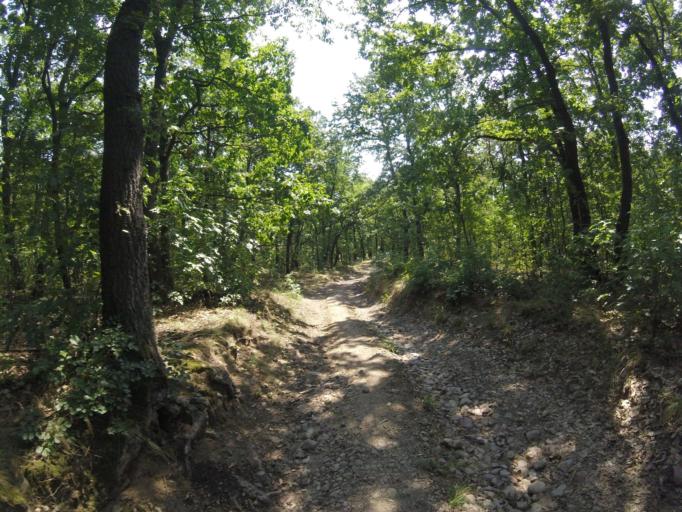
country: HU
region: Pest
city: Csobanka
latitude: 47.6729
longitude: 18.9636
